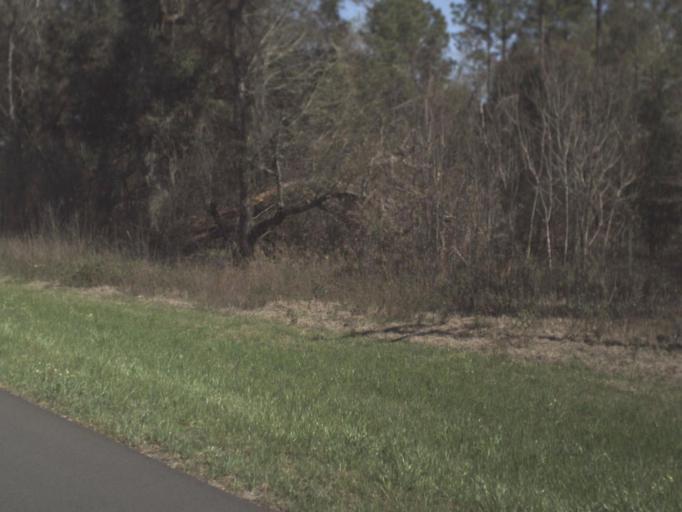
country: US
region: Florida
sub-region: Jackson County
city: Sneads
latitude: 30.7357
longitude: -85.0198
